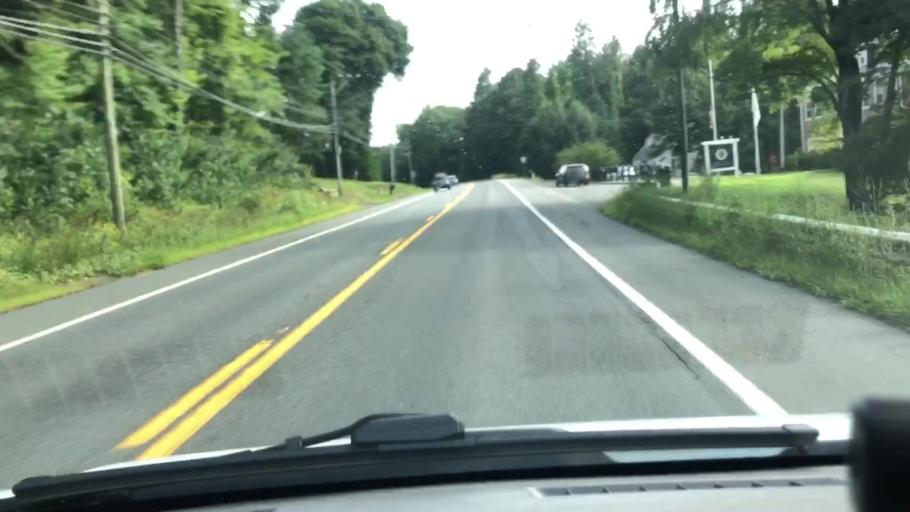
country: US
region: Massachusetts
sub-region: Franklin County
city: Shelburne Falls
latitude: 42.5961
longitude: -72.7281
